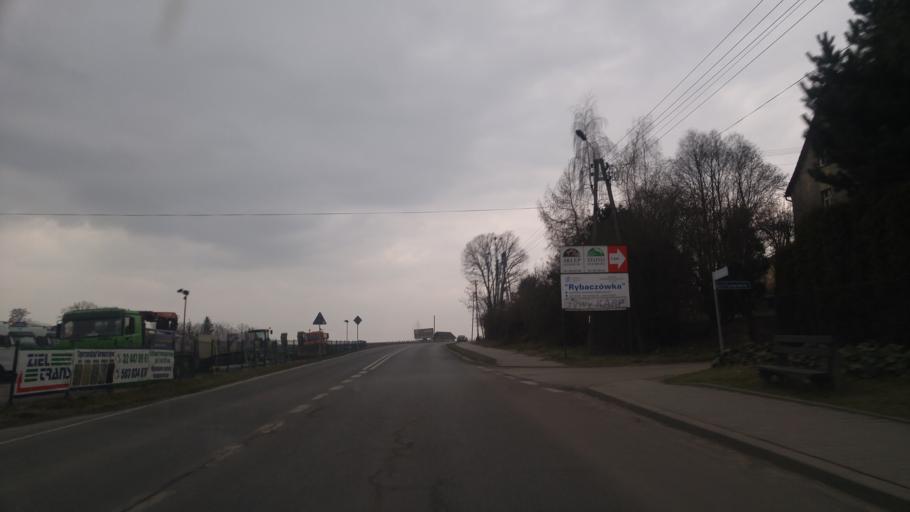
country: PL
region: Silesian Voivodeship
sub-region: Powiat pszczynski
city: Radostowice
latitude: 49.9560
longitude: 18.9038
